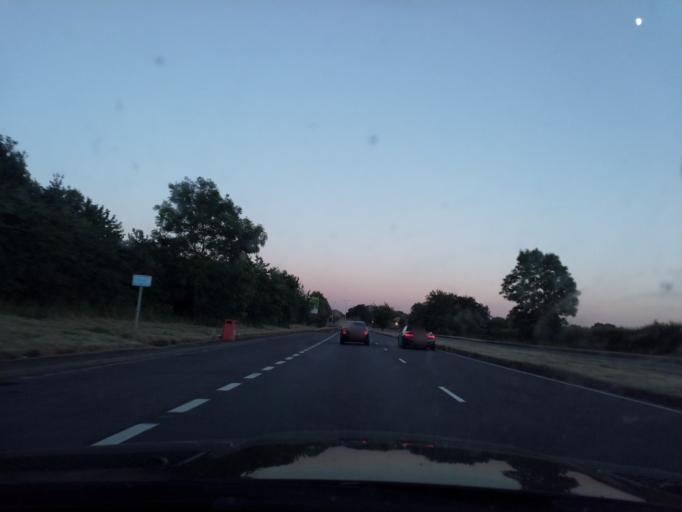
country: GB
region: England
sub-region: Solihull
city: Barston
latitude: 52.4160
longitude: -1.6758
